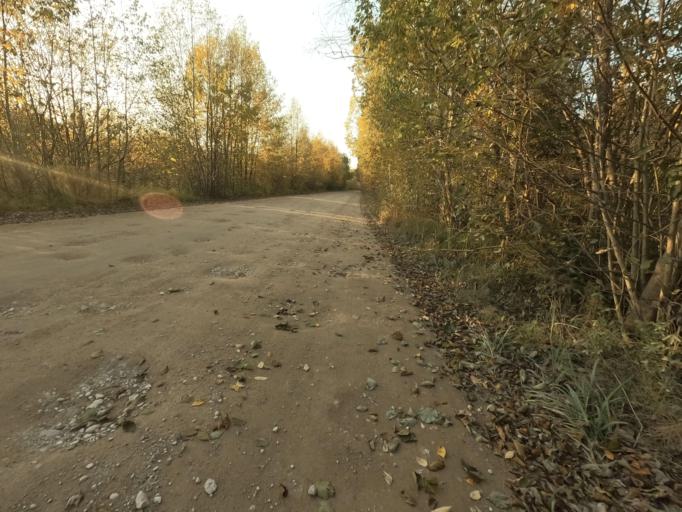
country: RU
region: Leningrad
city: Lyuban'
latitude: 59.0003
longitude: 31.1008
